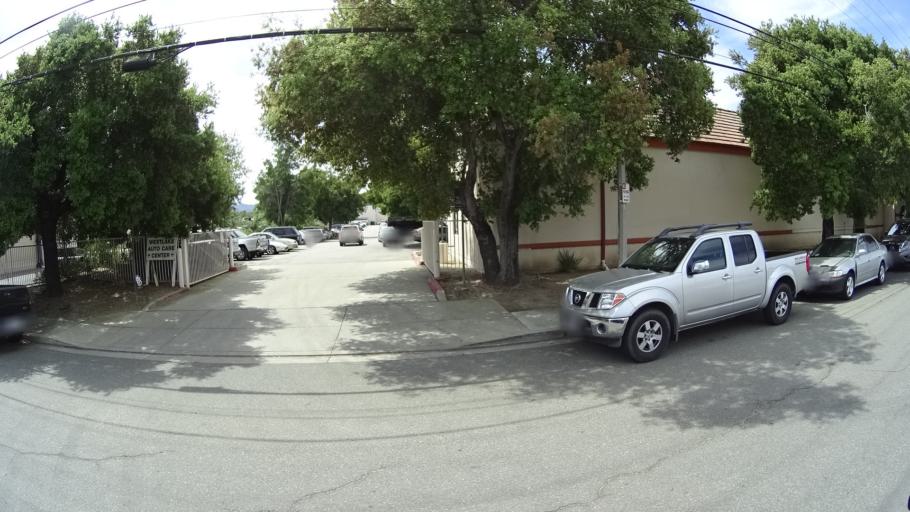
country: US
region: California
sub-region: Ventura County
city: Thousand Oaks
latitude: 34.1704
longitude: -118.8340
